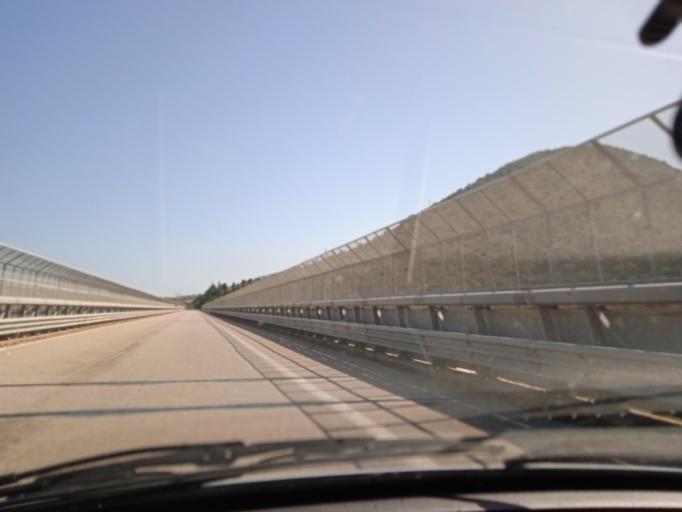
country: IT
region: Sicily
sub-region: Messina
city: Rocca di Capri Leone
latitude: 38.1093
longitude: 14.7223
